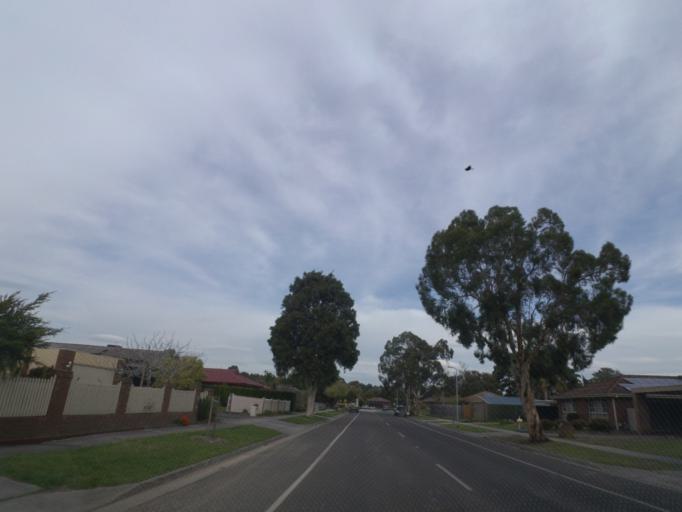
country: AU
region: Victoria
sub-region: Knox
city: Knoxfield
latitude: -37.8932
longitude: 145.2671
